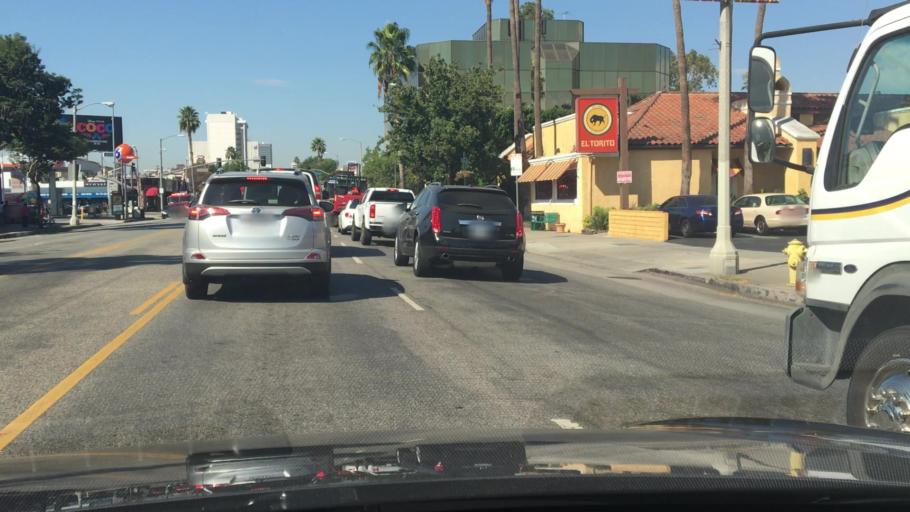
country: US
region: California
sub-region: Los Angeles County
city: Sherman Oaks
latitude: 34.1507
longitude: -118.4473
